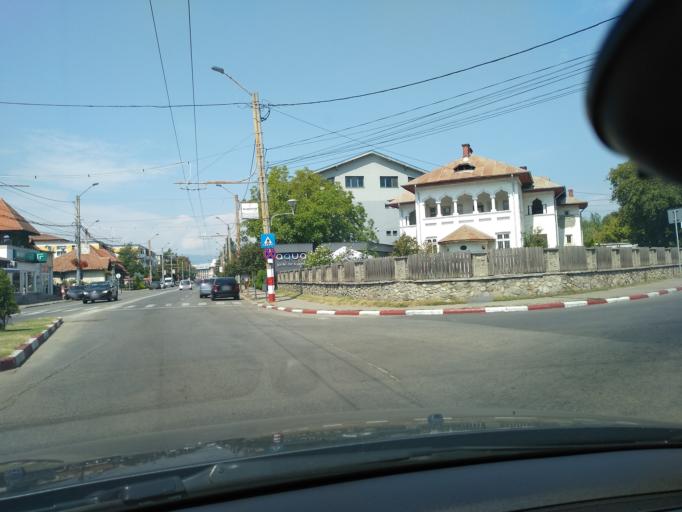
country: RO
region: Gorj
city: Targu Jiu
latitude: 45.0336
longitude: 23.2786
